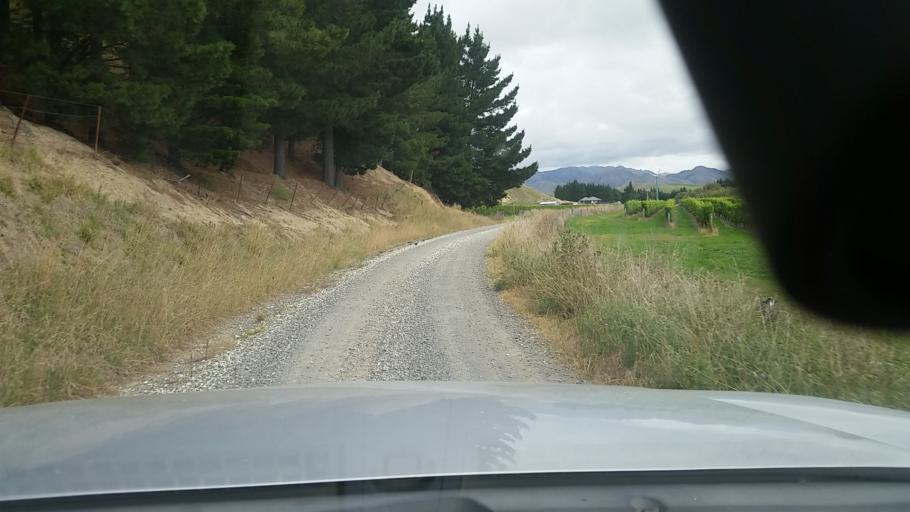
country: NZ
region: Marlborough
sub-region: Marlborough District
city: Blenheim
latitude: -41.6954
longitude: 174.1241
